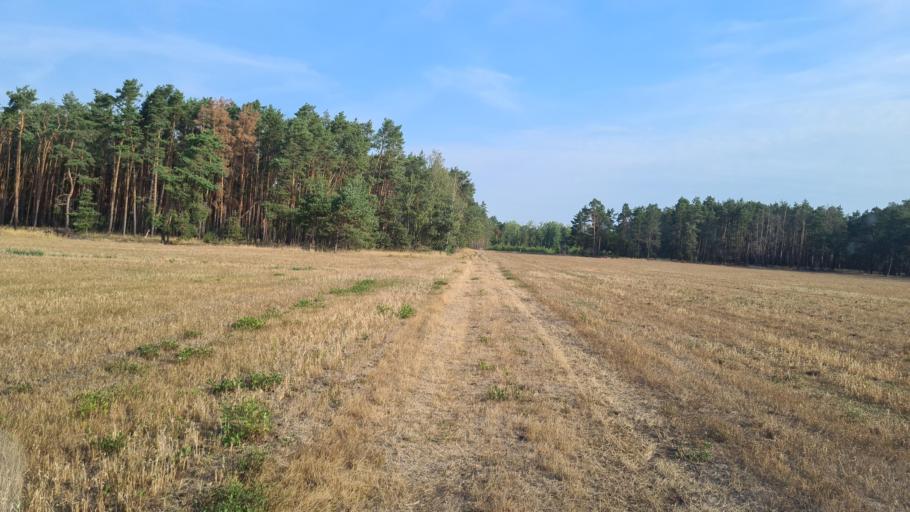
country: DE
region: Brandenburg
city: Finsterwalde
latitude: 51.6540
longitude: 13.7706
